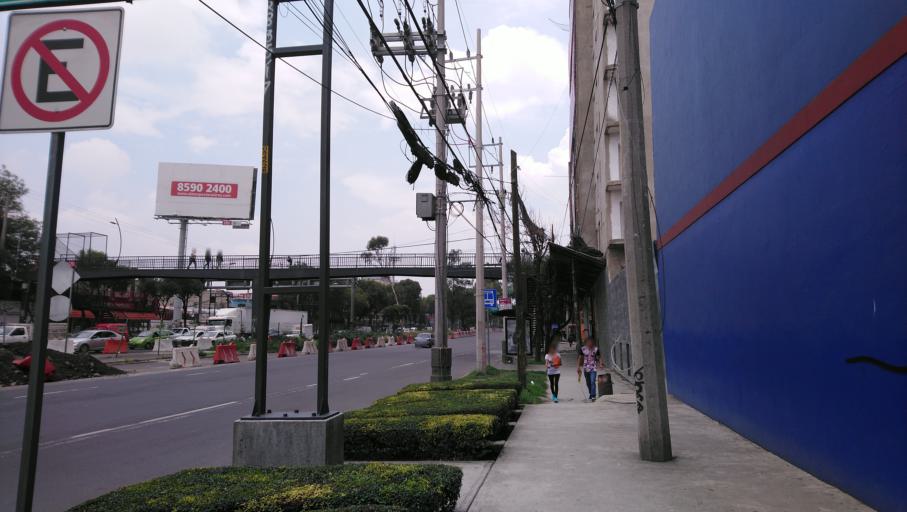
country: MX
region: Mexico City
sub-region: Iztacalco
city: Iztacalco
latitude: 19.4012
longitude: -99.1135
